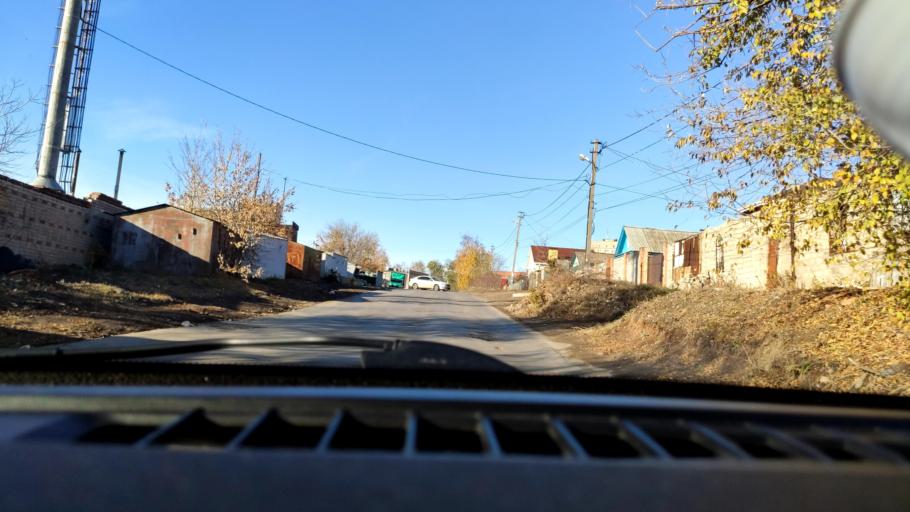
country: RU
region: Samara
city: Samara
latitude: 53.1845
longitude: 50.1791
